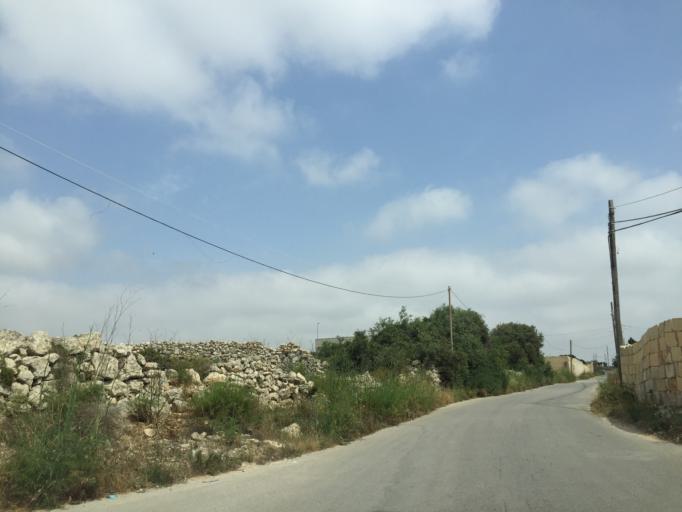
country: MT
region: L-Imgarr
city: Imgarr
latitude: 35.9002
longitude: 14.3522
